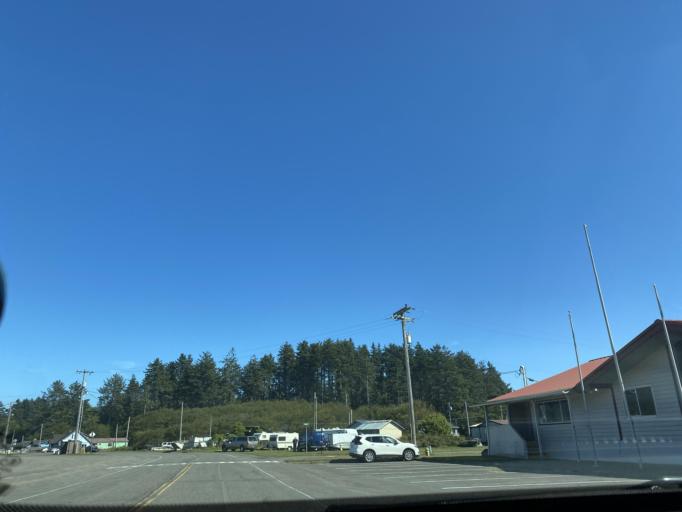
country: US
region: Washington
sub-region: Clallam County
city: Forks
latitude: 47.9098
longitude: -124.6367
